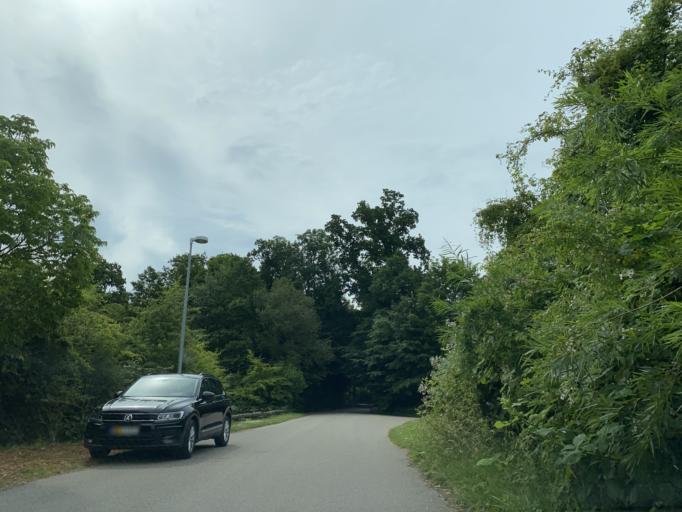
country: DK
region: South Denmark
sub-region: Sonderborg Kommune
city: Sonderborg
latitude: 54.9116
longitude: 9.8298
